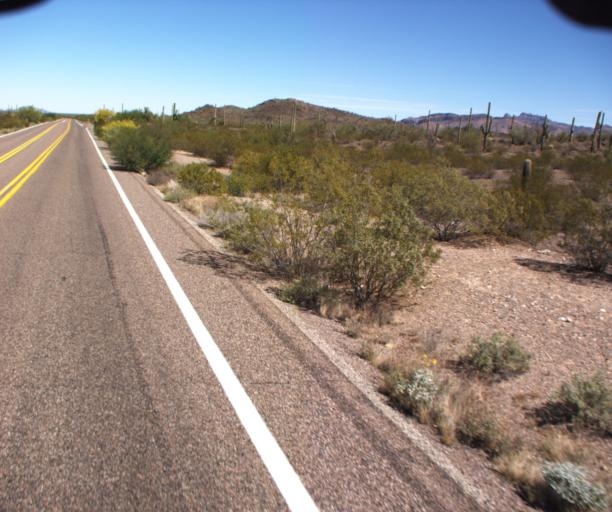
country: MX
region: Sonora
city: Sonoyta
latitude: 31.9900
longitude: -112.8061
